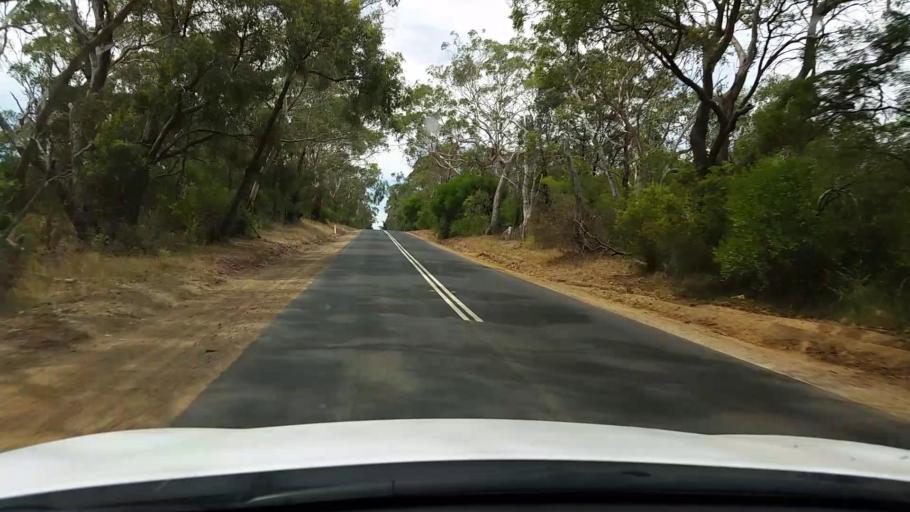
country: AU
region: Victoria
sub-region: Mornington Peninsula
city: Mount Martha
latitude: -38.2939
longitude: 145.0496
